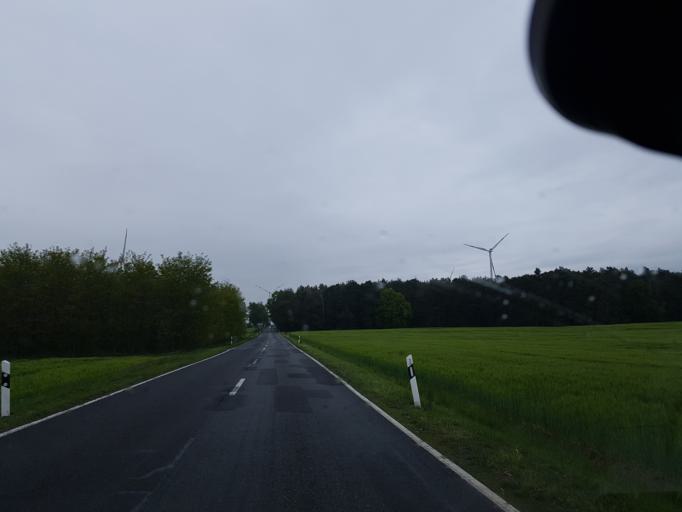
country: DE
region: Brandenburg
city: Drebkau
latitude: 51.6431
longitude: 14.2781
